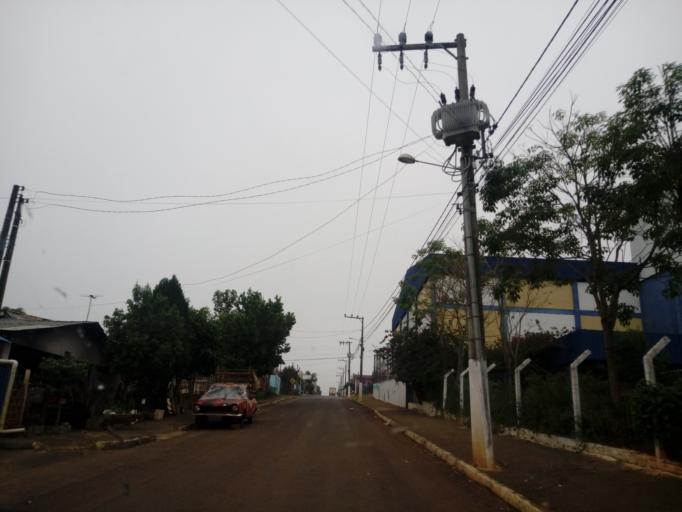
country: BR
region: Santa Catarina
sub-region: Chapeco
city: Chapeco
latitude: -27.1066
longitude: -52.6766
